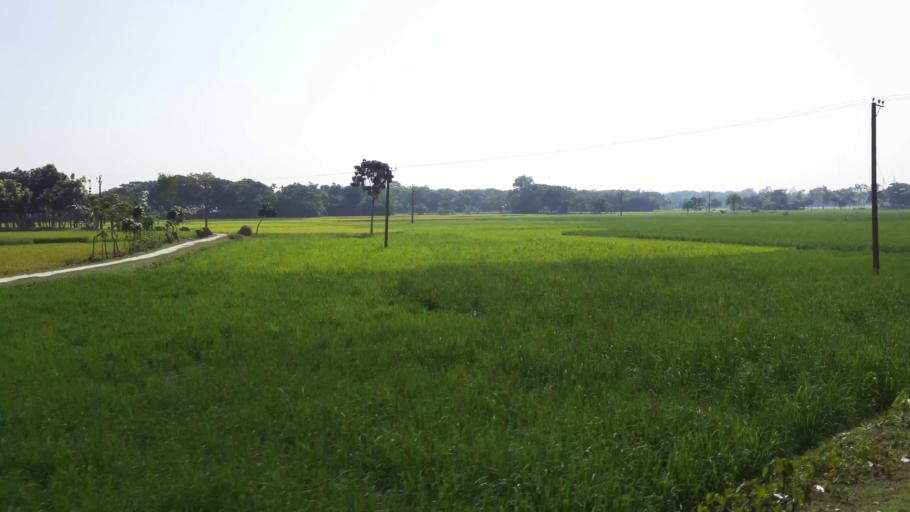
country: BD
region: Dhaka
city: Gafargaon
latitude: 24.5748
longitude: 90.5081
